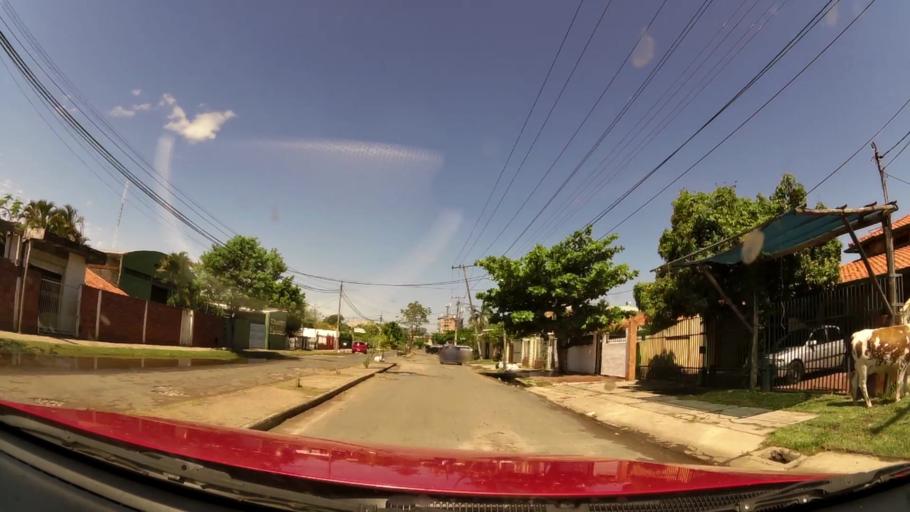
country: PY
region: Central
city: Colonia Mariano Roque Alonso
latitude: -25.2244
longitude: -57.5366
